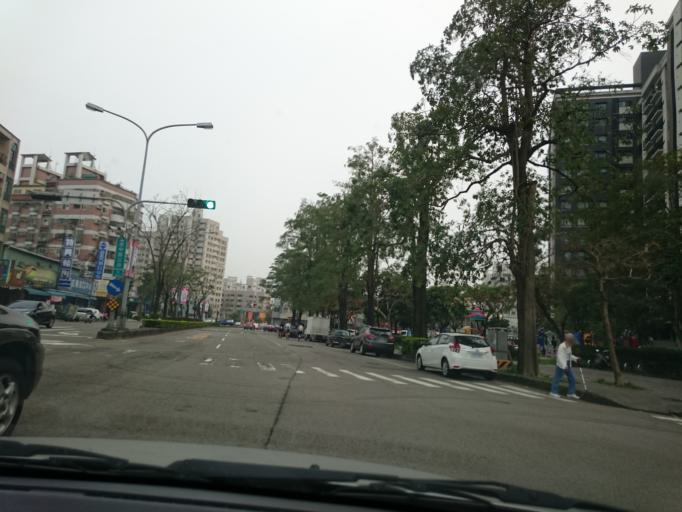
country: TW
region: Taiwan
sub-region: Taichung City
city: Taichung
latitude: 24.1427
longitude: 120.6406
